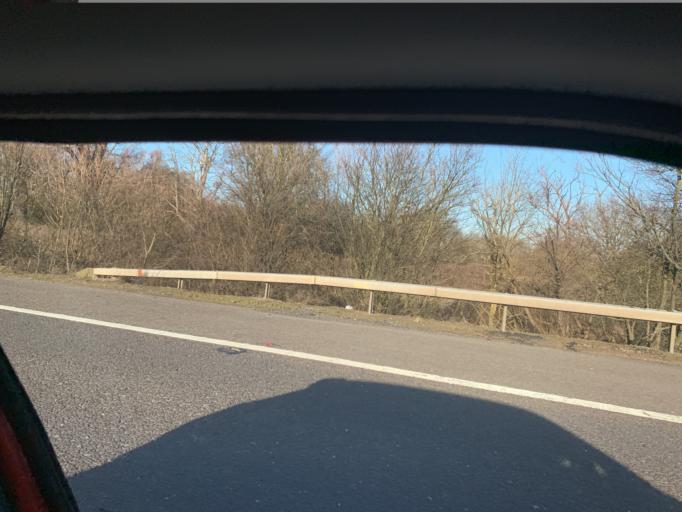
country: GB
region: England
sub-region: Surrey
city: Chertsey
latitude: 51.3828
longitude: -0.5158
